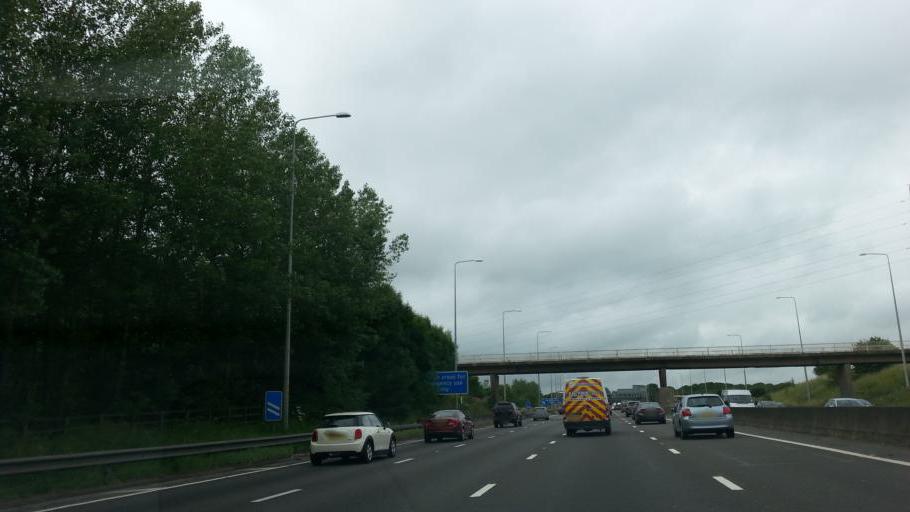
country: GB
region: England
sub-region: Kirklees
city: Cleckheaton
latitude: 53.7065
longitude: -1.7437
